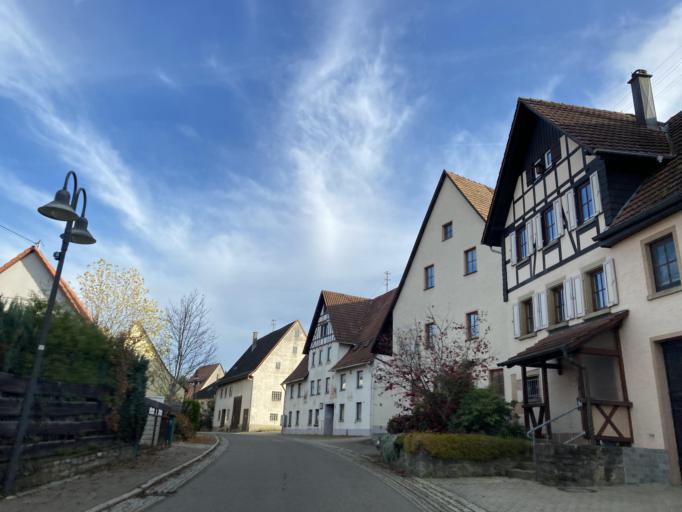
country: DE
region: Baden-Wuerttemberg
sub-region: Regierungsbezirk Stuttgart
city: Bondorf
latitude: 48.4729
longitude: 8.8163
